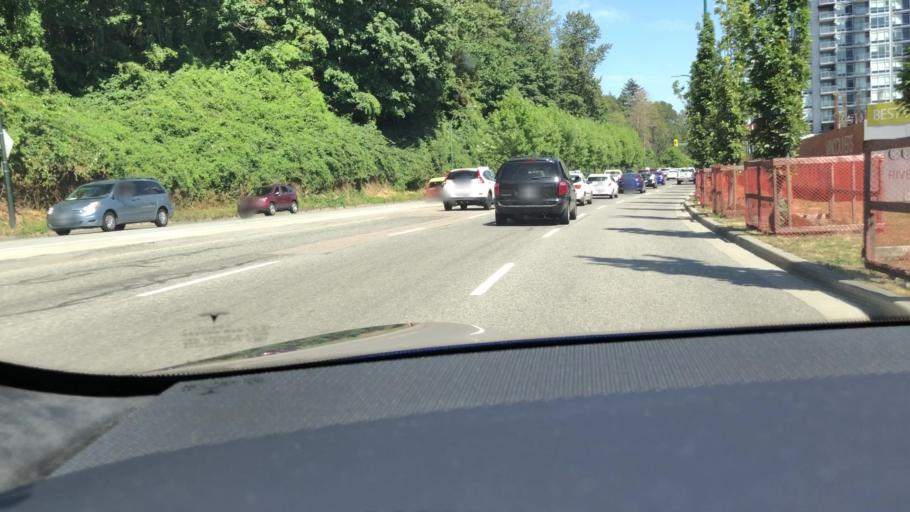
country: CA
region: British Columbia
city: Vancouver
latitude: 49.2070
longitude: -123.0332
